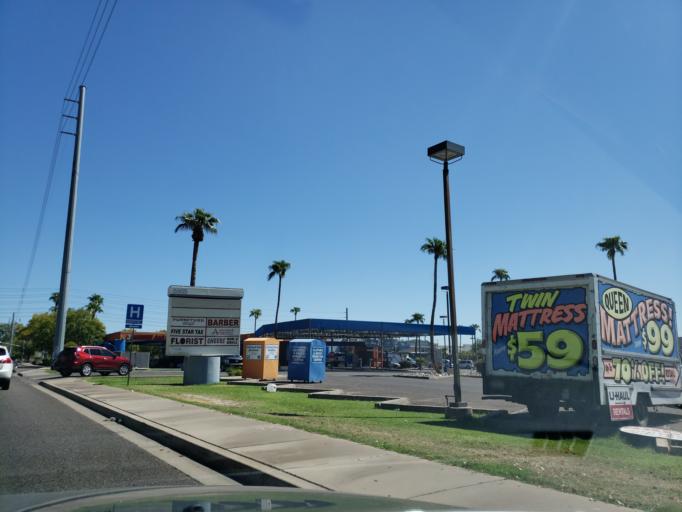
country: US
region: Arizona
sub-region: Maricopa County
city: Peoria
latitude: 33.6383
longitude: -112.1880
